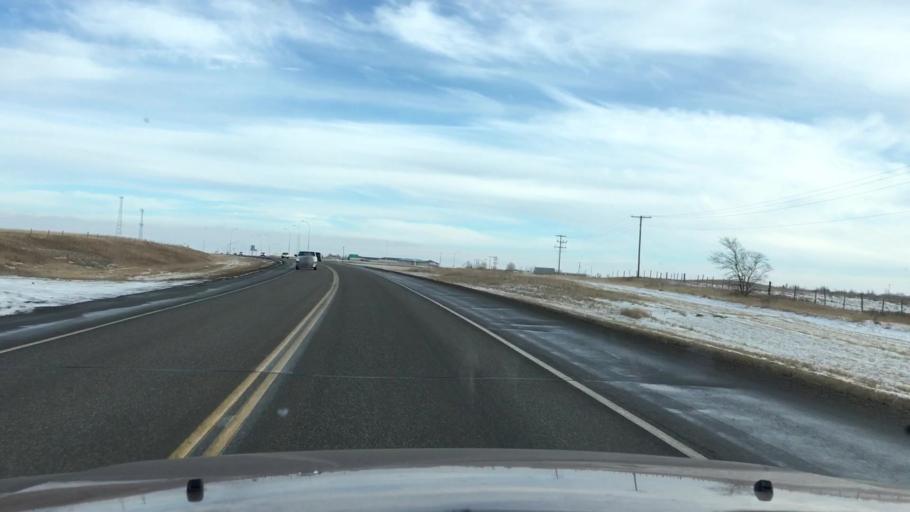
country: CA
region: Saskatchewan
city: Pilot Butte
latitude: 50.4844
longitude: -104.4415
